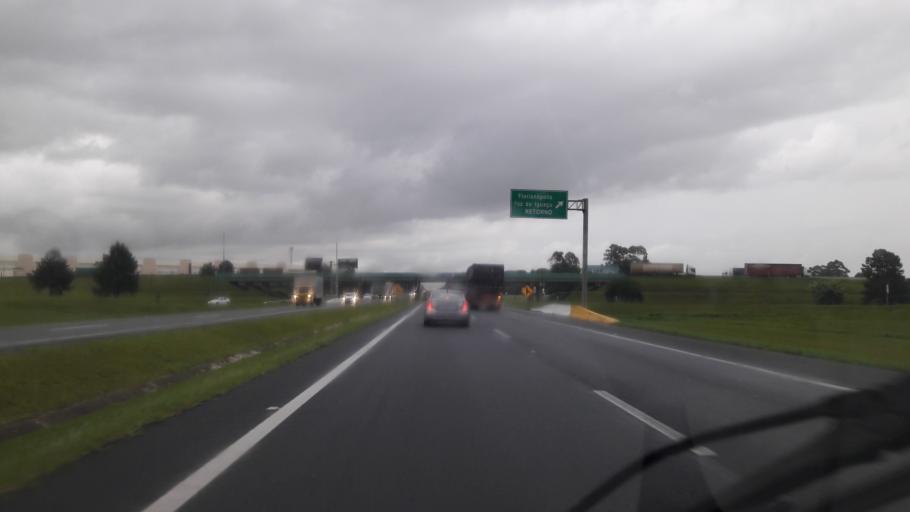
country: BR
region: Parana
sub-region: Sao Jose Dos Pinhais
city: Sao Jose dos Pinhais
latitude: -25.5118
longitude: -49.1258
